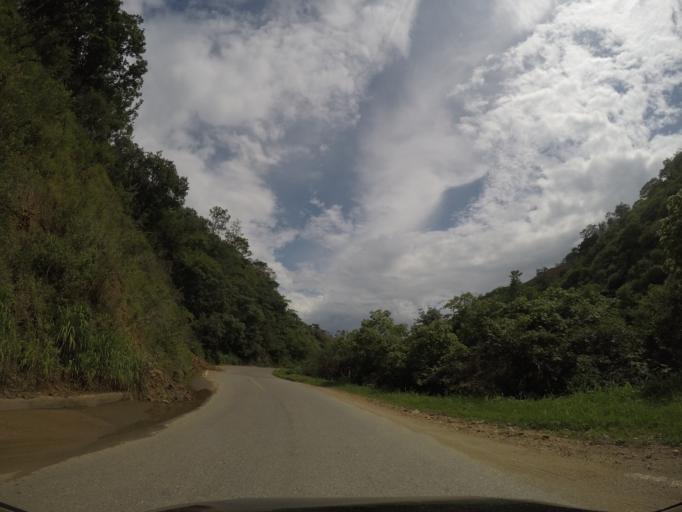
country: MX
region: Oaxaca
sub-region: San Jeronimo Coatlan
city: San Cristobal Honduras
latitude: 16.3865
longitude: -97.0759
